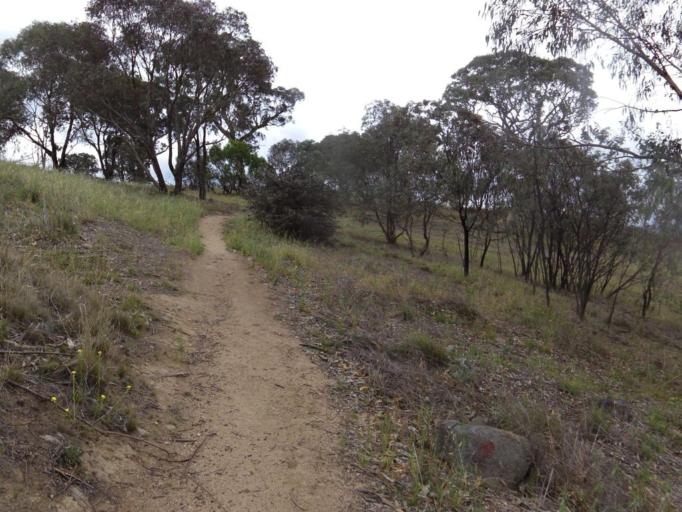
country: AU
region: Australian Capital Territory
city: Forrest
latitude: -35.3582
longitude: 149.0298
